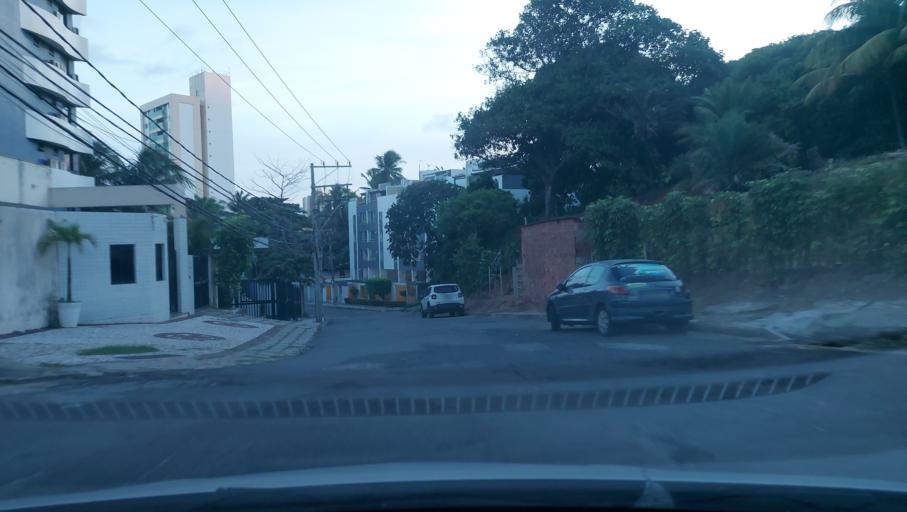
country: BR
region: Bahia
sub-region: Salvador
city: Salvador
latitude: -12.9880
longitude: -38.4398
